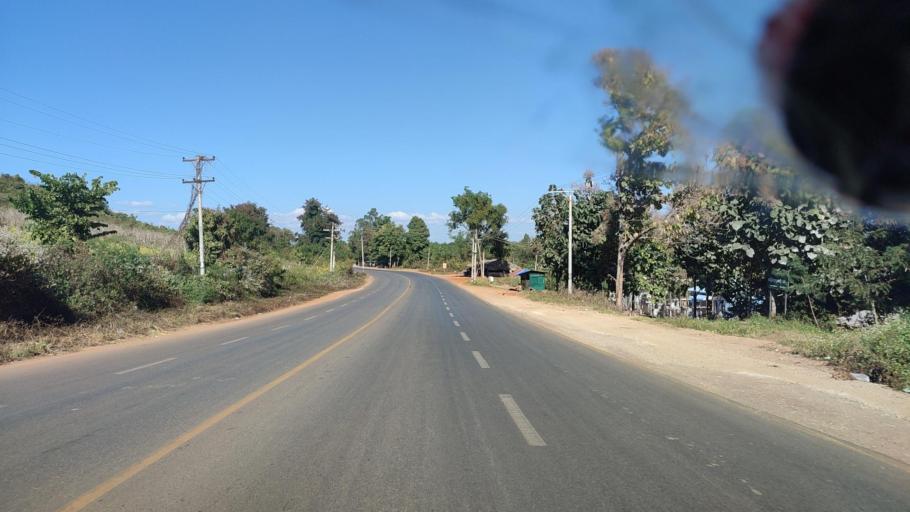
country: MM
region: Mandalay
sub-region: Pyin Oo Lwin District
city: Pyin Oo Lwin
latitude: 22.0964
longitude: 96.5965
